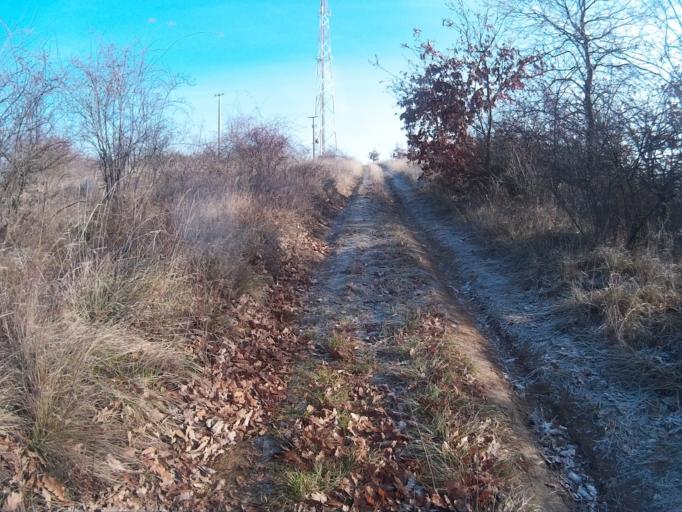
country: HU
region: Nograd
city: Bercel
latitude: 47.9316
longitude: 19.4150
